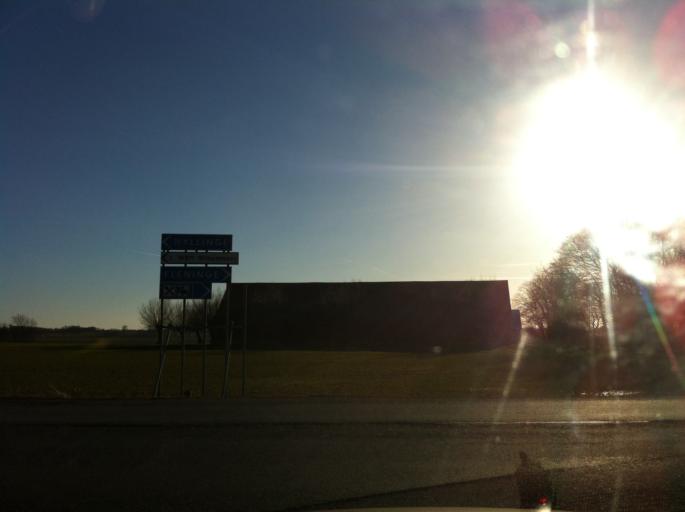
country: SE
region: Skane
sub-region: Angelholms Kommun
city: Strovelstorp
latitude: 56.1049
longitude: 12.8021
